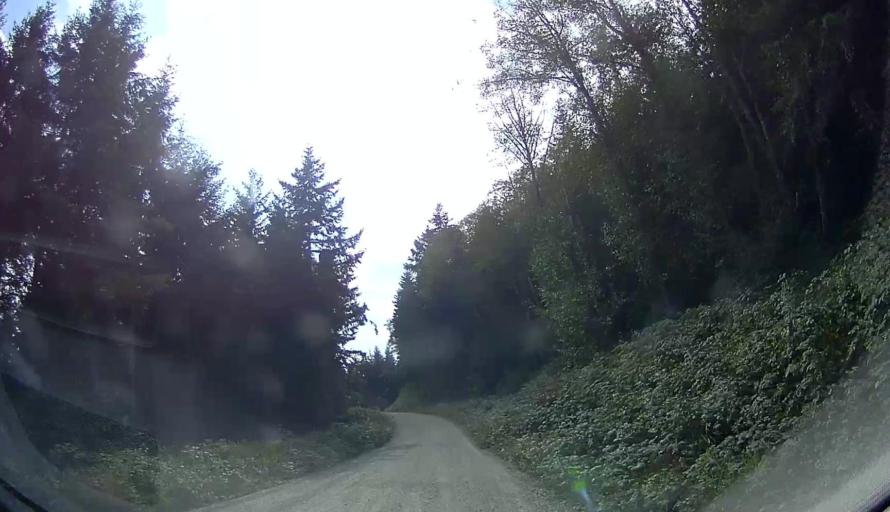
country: US
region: Washington
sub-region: Whatcom County
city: Sudden Valley
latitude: 48.6118
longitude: -122.3811
